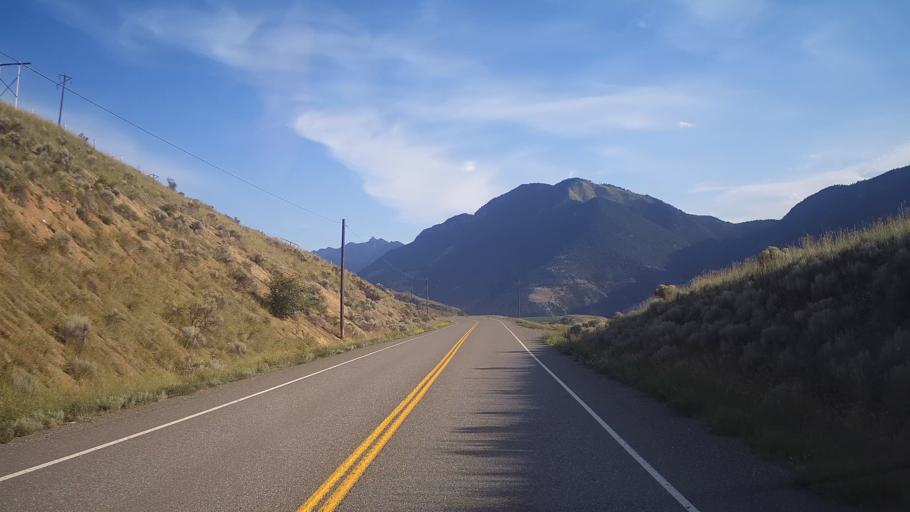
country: CA
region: British Columbia
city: Lillooet
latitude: 50.8436
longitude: -121.8616
